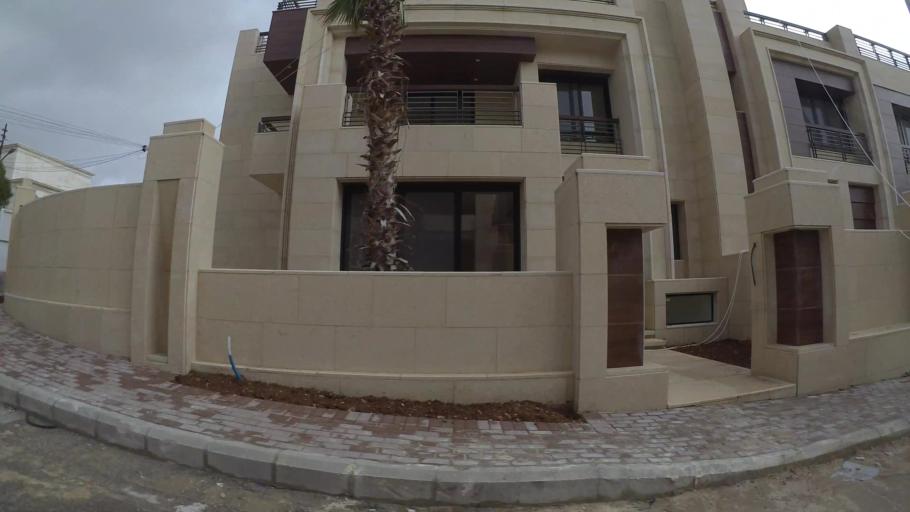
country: JO
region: Amman
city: Al Bunayyat ash Shamaliyah
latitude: 31.9520
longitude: 35.8802
